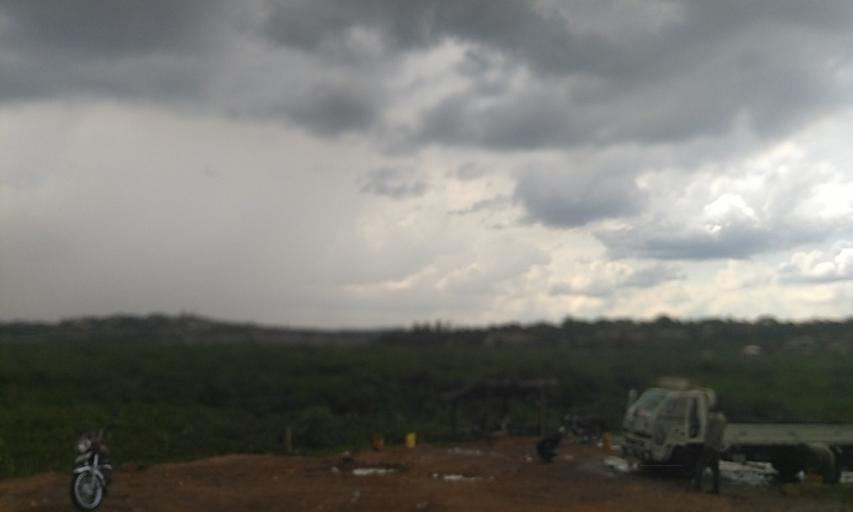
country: UG
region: Central Region
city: Kampala Central Division
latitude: 0.3132
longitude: 32.5133
